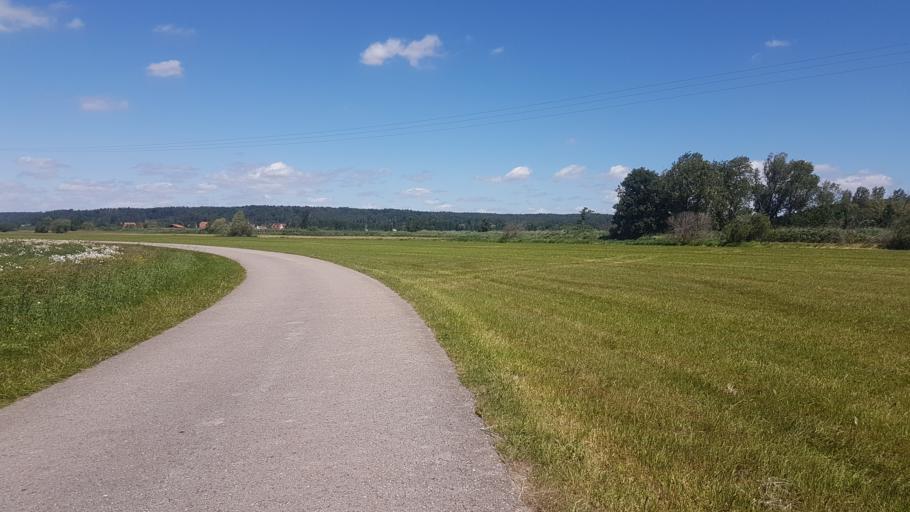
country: DE
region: Bavaria
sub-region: Regierungsbezirk Mittelfranken
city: Aurach
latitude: 49.2618
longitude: 10.4521
